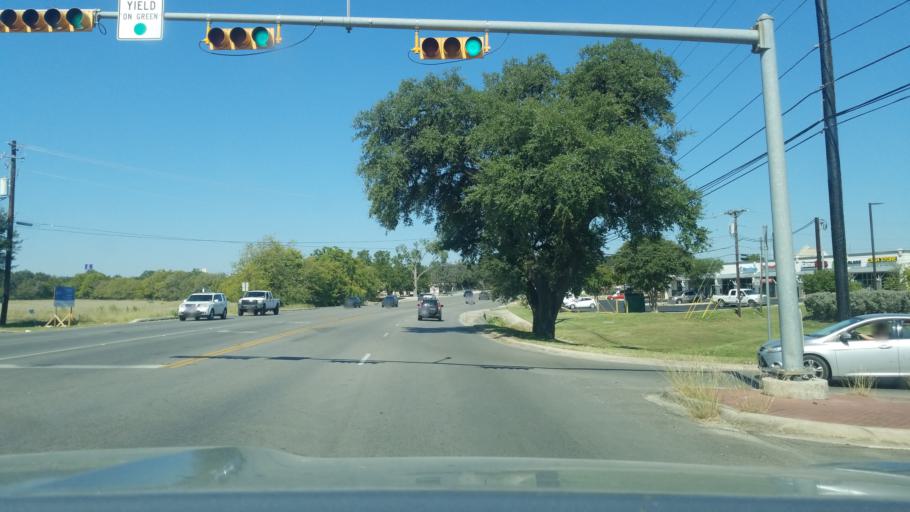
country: US
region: Texas
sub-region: Kendall County
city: Boerne
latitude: 29.7770
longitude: -98.7262
